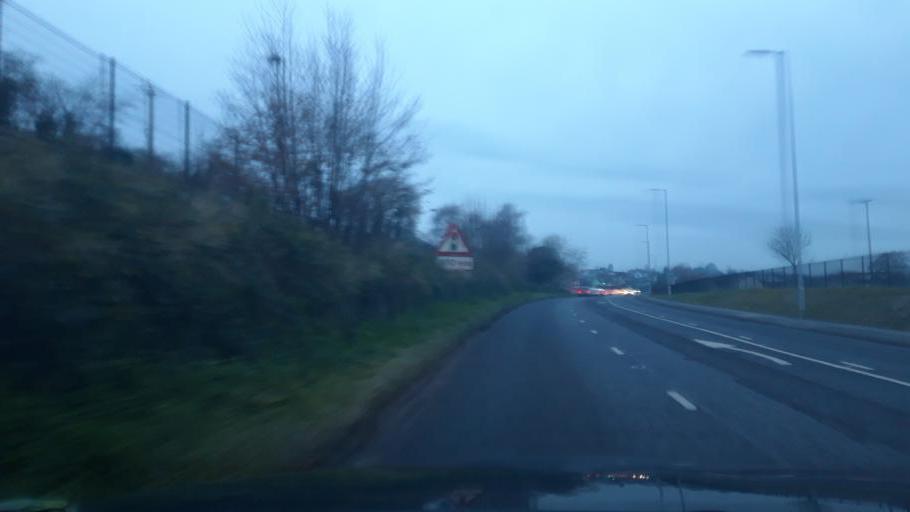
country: GB
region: Northern Ireland
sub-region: Newry and Mourne District
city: Newry
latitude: 54.1827
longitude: -6.3542
